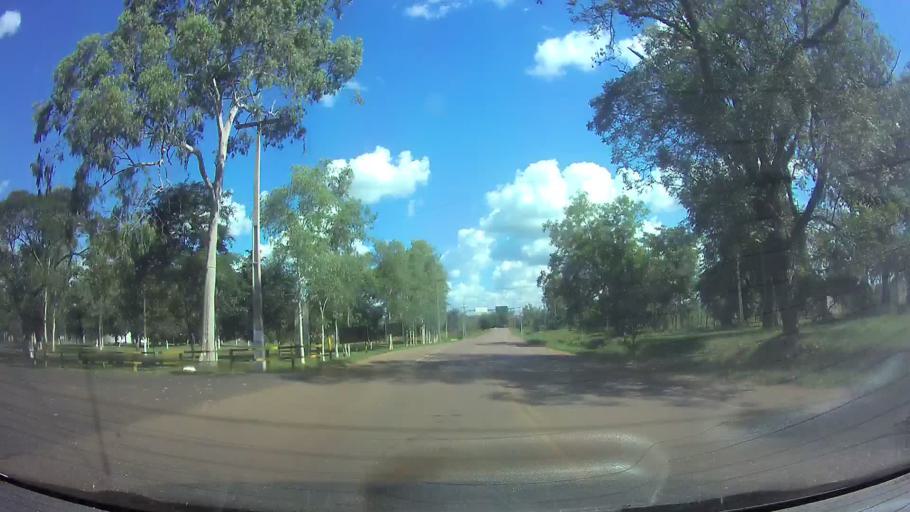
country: PY
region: Guaira
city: Coronel Martinez
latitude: -25.7706
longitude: -56.6519
